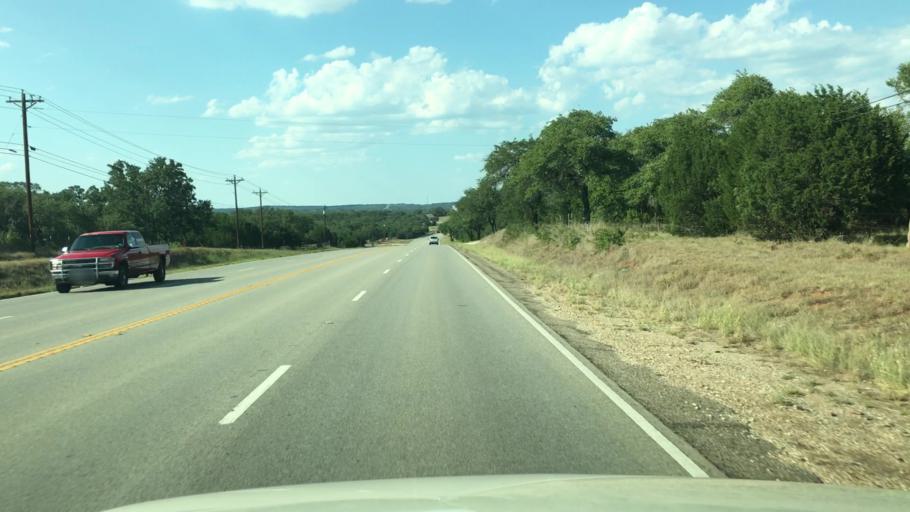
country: US
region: Texas
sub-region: Blanco County
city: Johnson City
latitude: 30.3049
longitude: -98.3950
